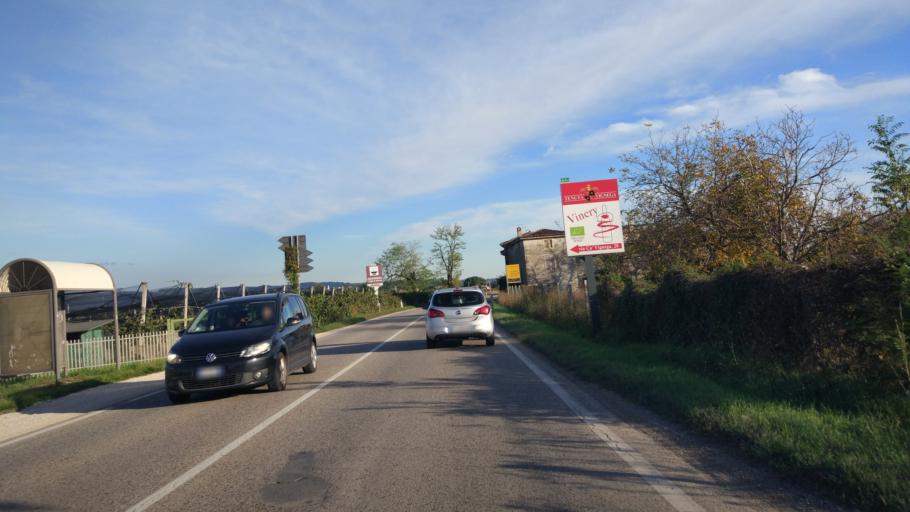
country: IT
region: Veneto
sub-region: Provincia di Verona
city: Ospedaletto
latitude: 45.5039
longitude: 10.8496
